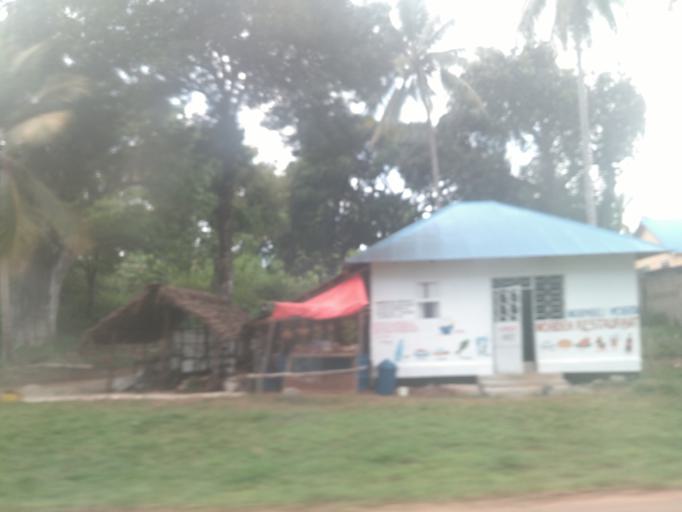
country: TZ
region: Zanzibar Urban/West
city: Zanzibar
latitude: -6.2771
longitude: 39.2730
